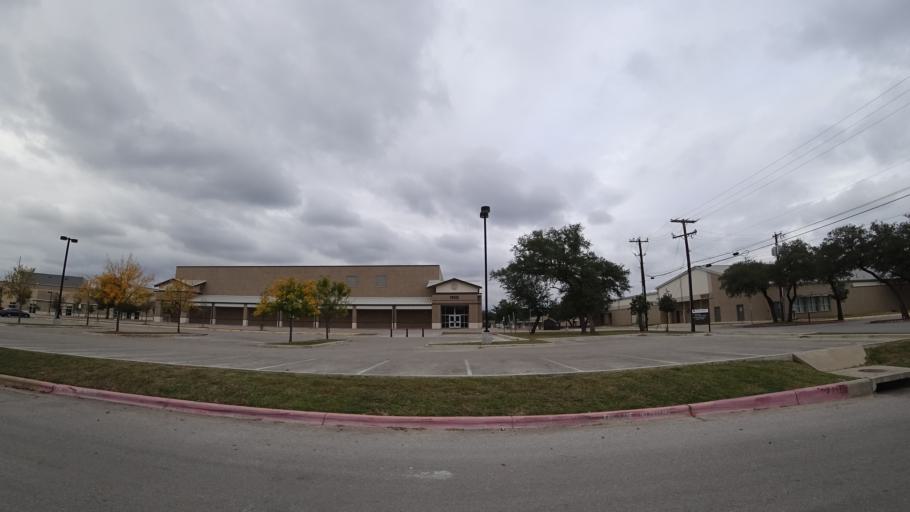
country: US
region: Texas
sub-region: Williamson County
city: Round Rock
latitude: 30.5078
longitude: -97.6980
